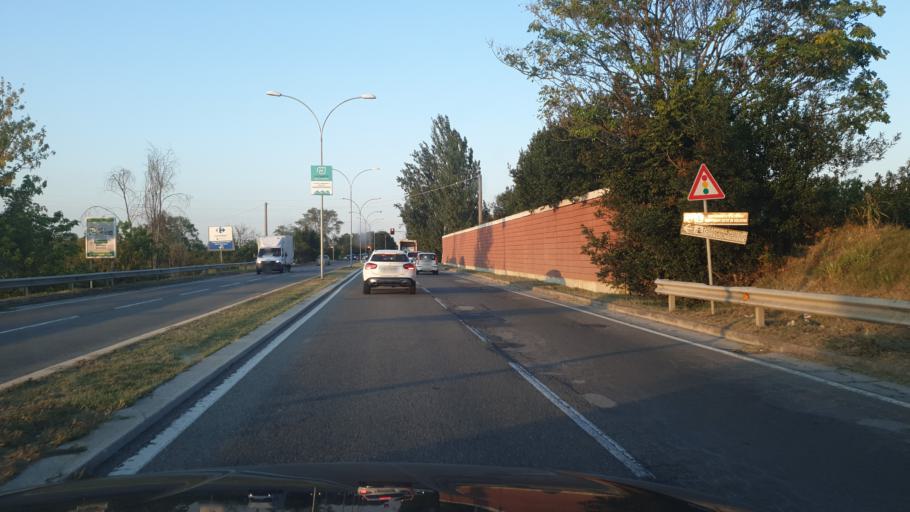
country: IT
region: Emilia-Romagna
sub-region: Provincia di Bologna
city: Quarto Inferiore
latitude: 44.5169
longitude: 11.3806
